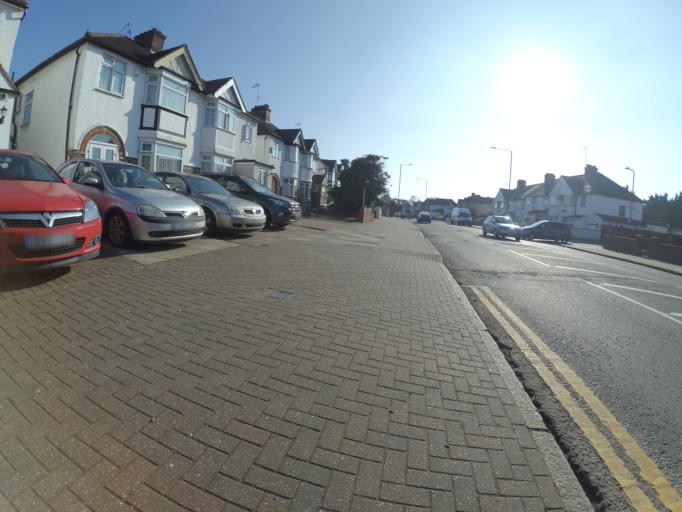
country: GB
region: England
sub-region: Greater London
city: Wembley
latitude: 51.5697
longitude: -0.2629
